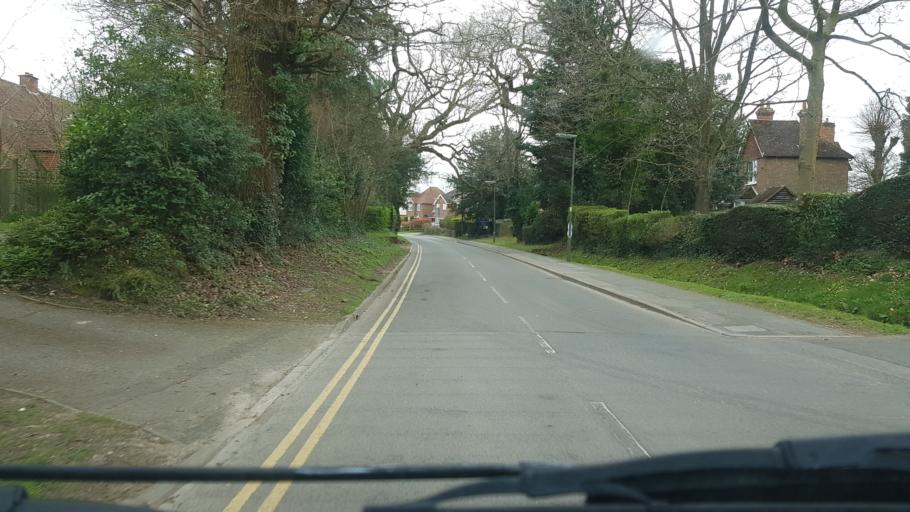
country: GB
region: England
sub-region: Surrey
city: Cranleigh
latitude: 51.1478
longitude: -0.4948
